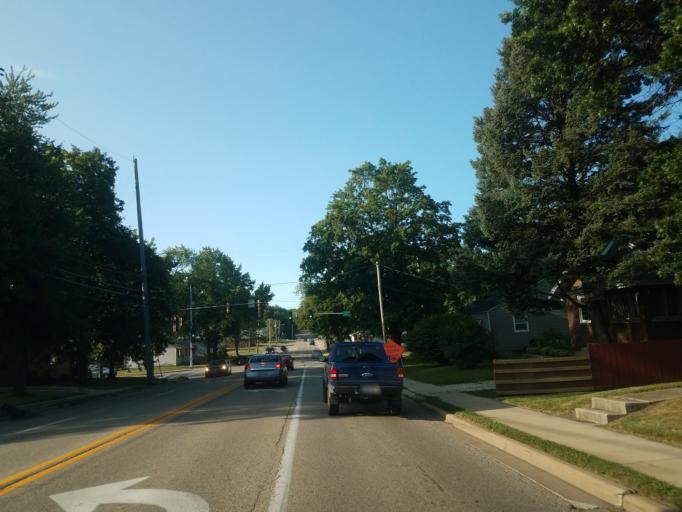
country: US
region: Illinois
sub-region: McLean County
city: Normal
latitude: 40.5055
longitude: -88.9823
